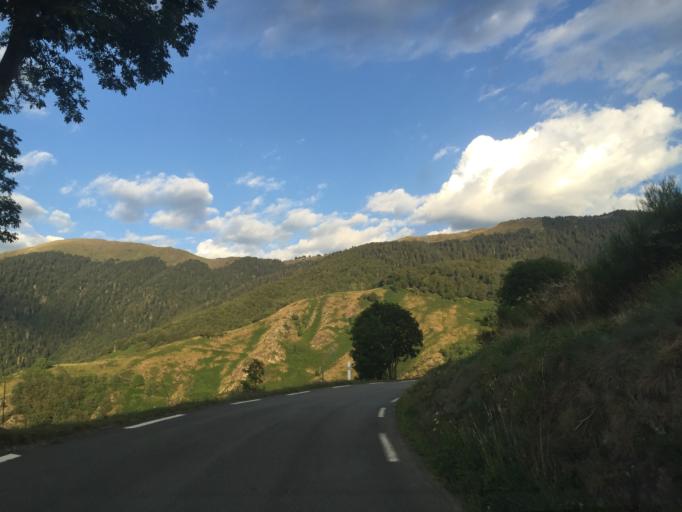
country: FR
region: Midi-Pyrenees
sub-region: Departement des Hautes-Pyrenees
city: Saint-Lary-Soulan
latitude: 42.9263
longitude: 0.3456
